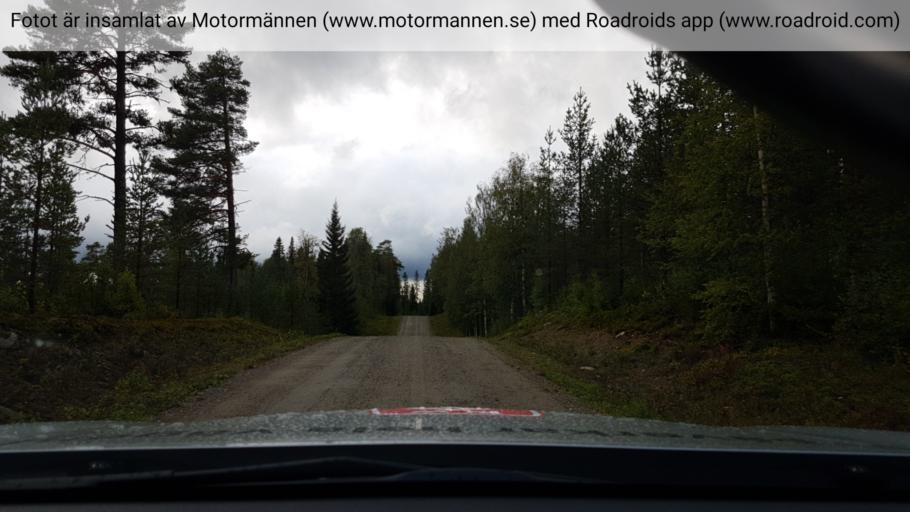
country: SE
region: Vaesterbotten
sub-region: Asele Kommun
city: Asele
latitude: 64.1482
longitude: 16.9363
